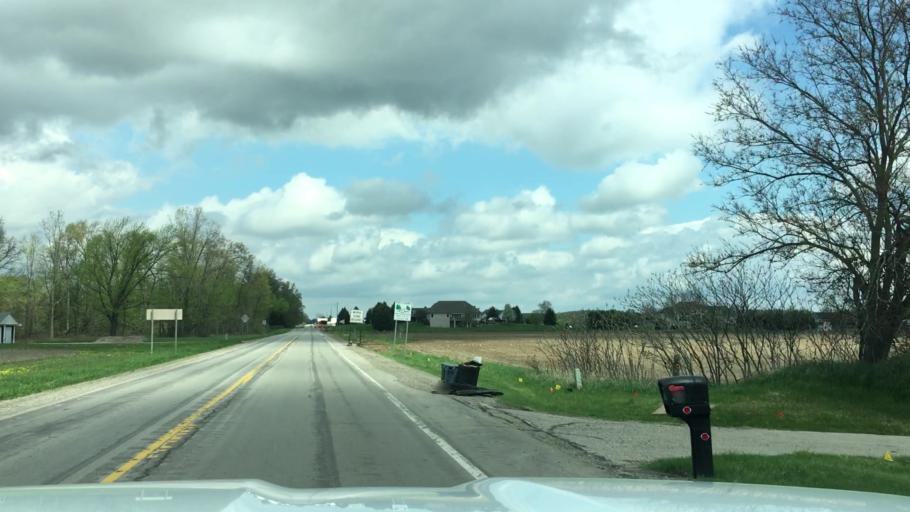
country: US
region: Michigan
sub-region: Ingham County
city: Stockbridge
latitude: 42.4552
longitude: -84.1901
